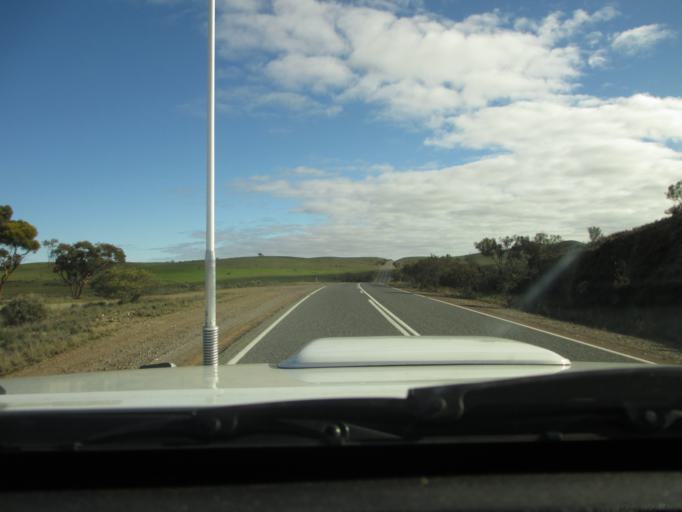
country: AU
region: South Australia
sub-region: Peterborough
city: Peterborough
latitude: -32.6207
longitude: 138.5787
